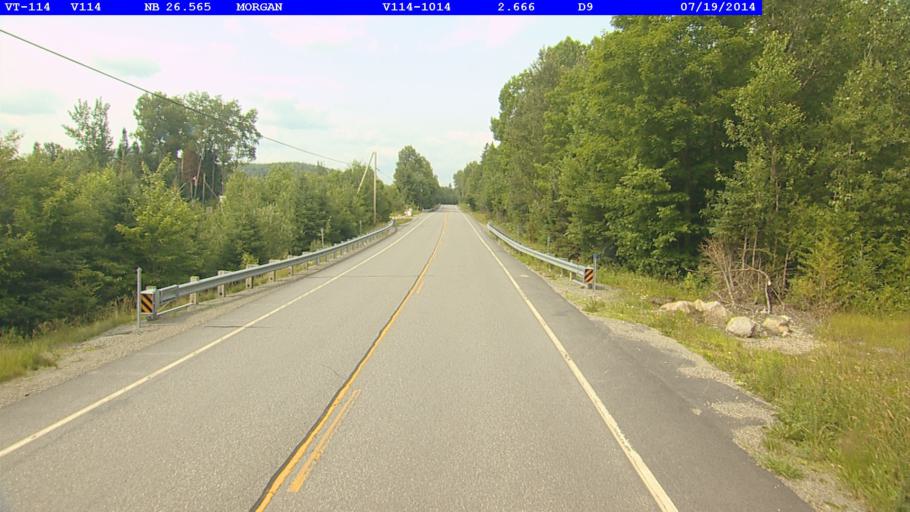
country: CA
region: Quebec
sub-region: Estrie
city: Coaticook
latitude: 44.8821
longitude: -71.8965
